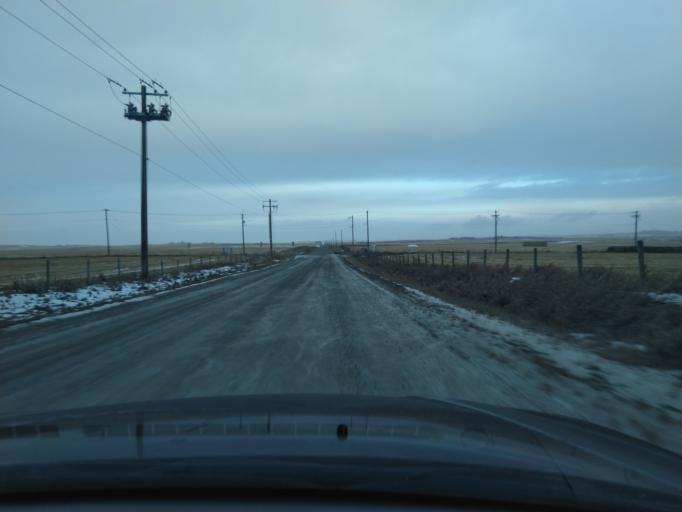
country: CA
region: Alberta
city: Airdrie
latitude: 51.1823
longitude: -114.0248
